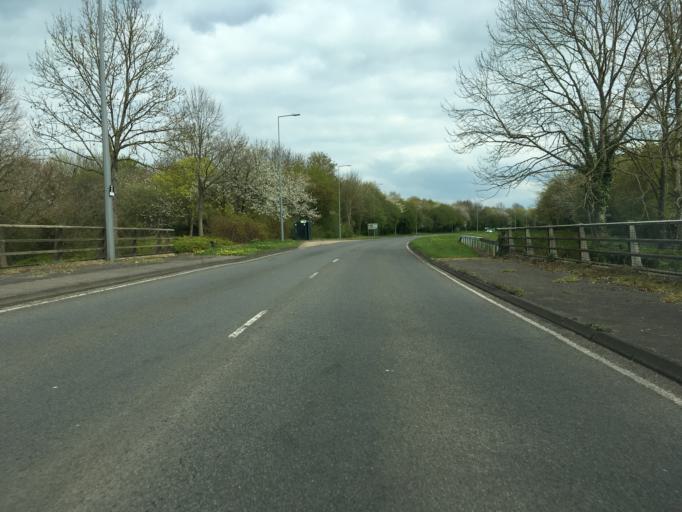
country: GB
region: England
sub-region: Milton Keynes
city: Bradwell
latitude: 52.0687
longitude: -0.7705
